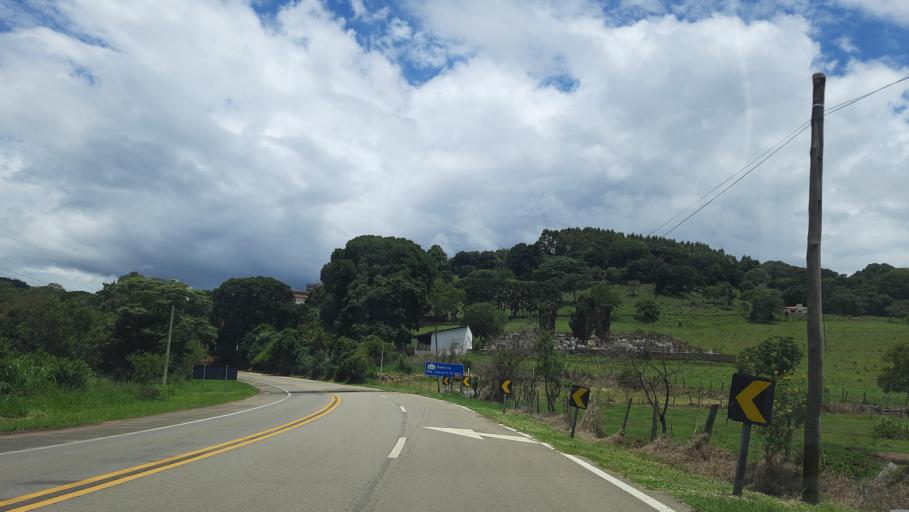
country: BR
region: Sao Paulo
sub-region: Sao Joao Da Boa Vista
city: Sao Joao da Boa Vista
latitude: -21.8353
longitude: -46.7494
